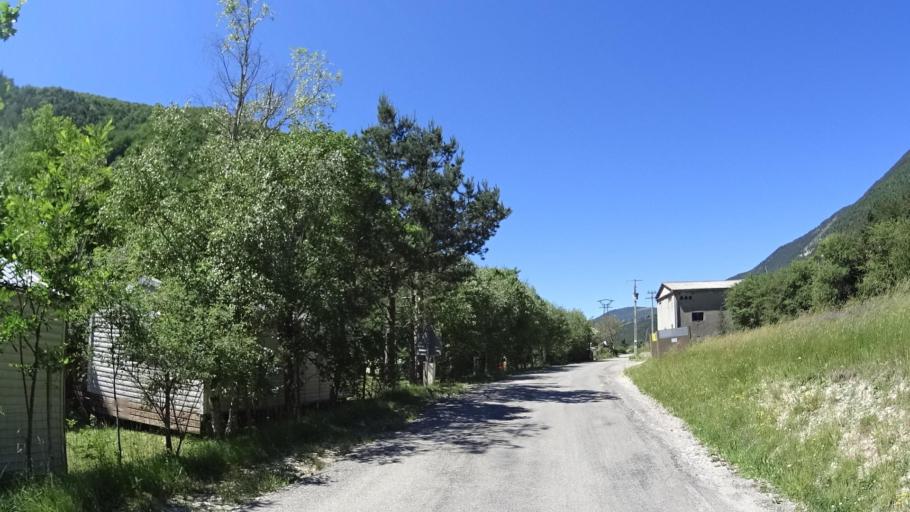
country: FR
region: Provence-Alpes-Cote d'Azur
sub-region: Departement des Alpes-de-Haute-Provence
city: Annot
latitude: 44.0073
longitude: 6.5593
